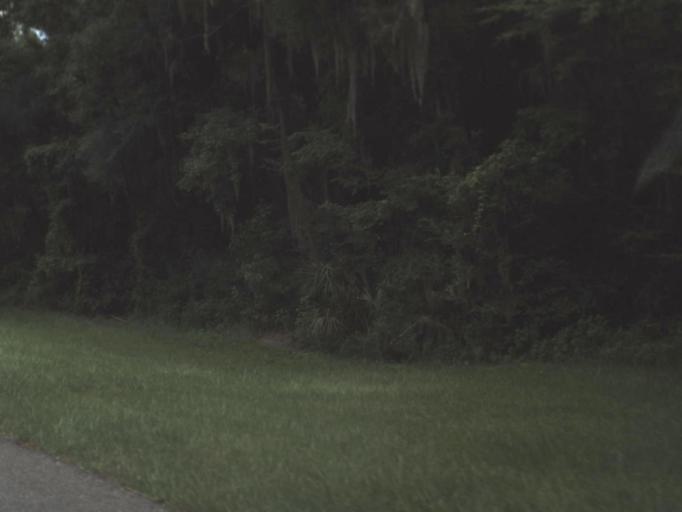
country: US
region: Florida
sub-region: Citrus County
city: Sugarmill Woods
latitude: 28.6642
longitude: -82.4686
